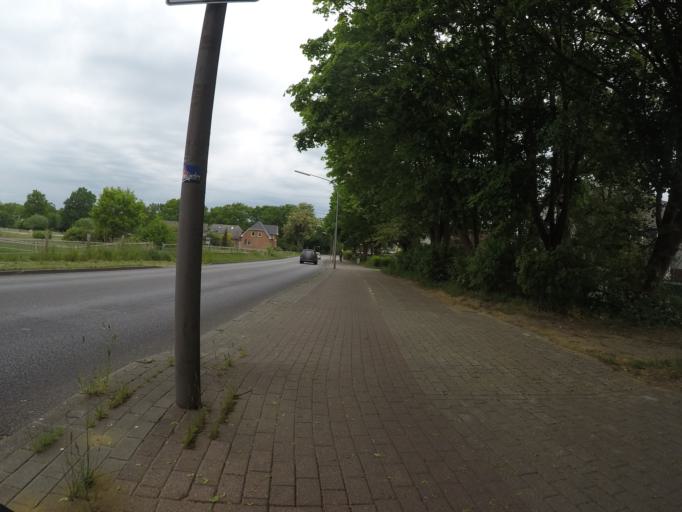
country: DE
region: Schleswig-Holstein
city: Norderstedt
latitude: 53.6850
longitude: 9.9745
